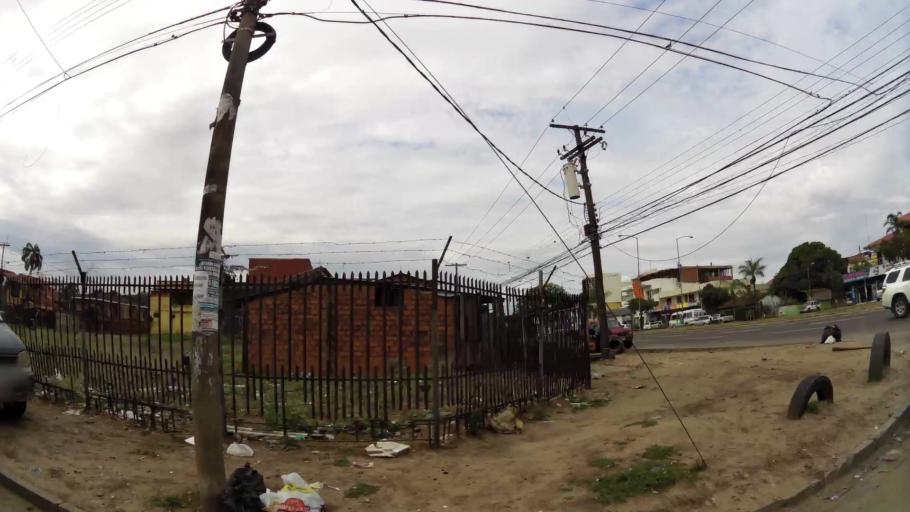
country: BO
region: Santa Cruz
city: Santa Cruz de la Sierra
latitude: -17.8031
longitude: -63.1987
